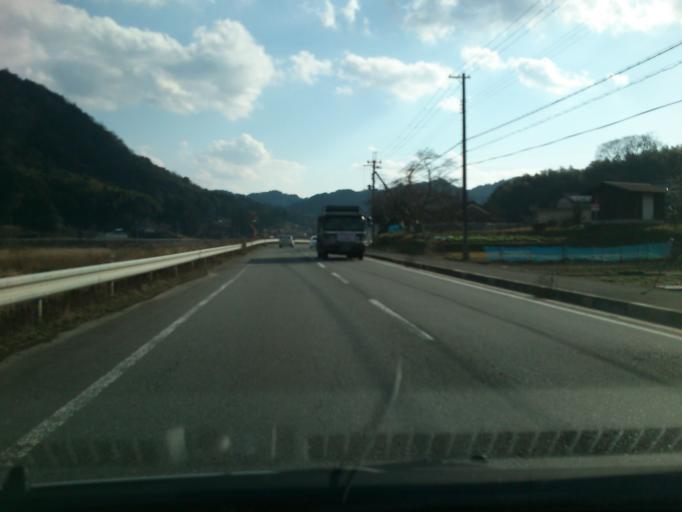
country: JP
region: Kyoto
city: Miyazu
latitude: 35.4155
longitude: 135.2021
